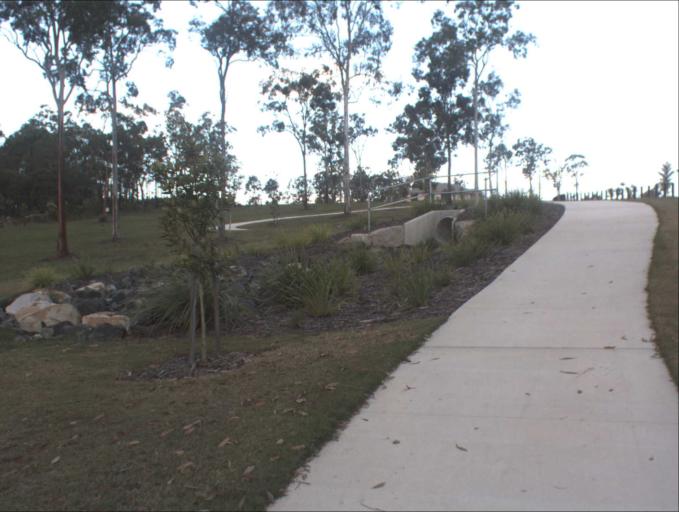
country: AU
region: Queensland
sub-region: Logan
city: North Maclean
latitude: -27.7454
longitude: 152.9421
